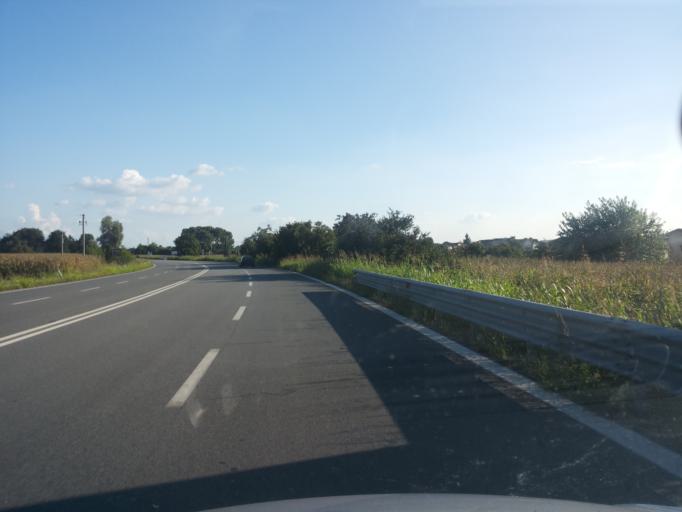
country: IT
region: Piedmont
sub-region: Provincia di Torino
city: Ivrea
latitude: 45.4409
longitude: 7.8832
